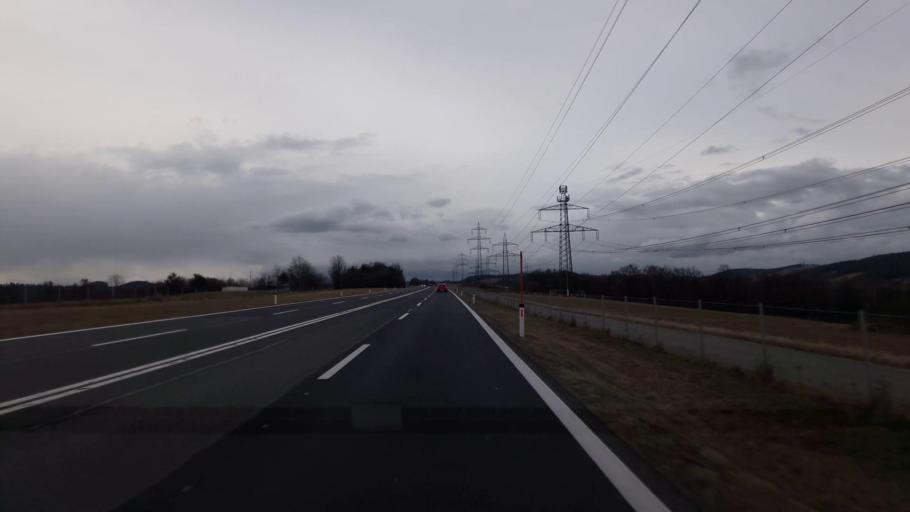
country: AT
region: Burgenland
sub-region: Politischer Bezirk Oberpullendorf
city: Kobersdorf
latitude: 47.6029
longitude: 16.4009
